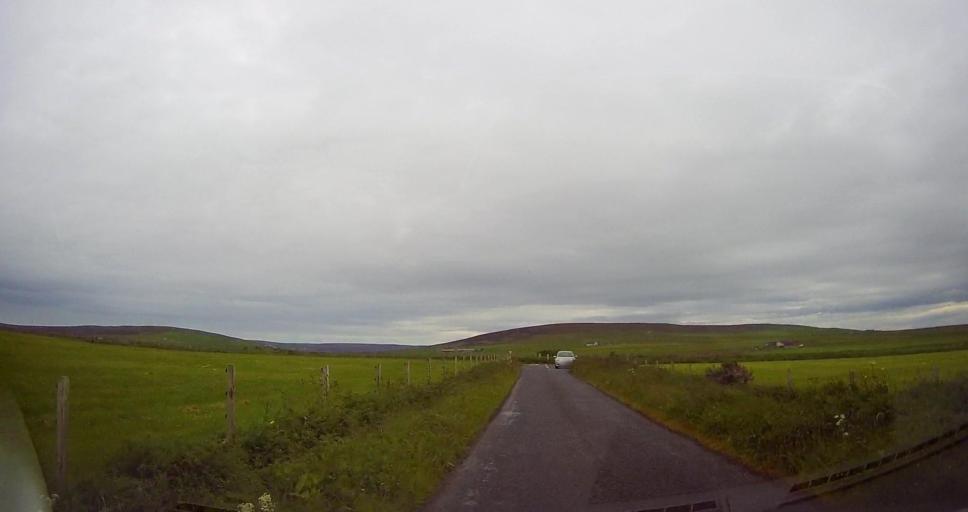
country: GB
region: Scotland
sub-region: Orkney Islands
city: Stromness
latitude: 59.1124
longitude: -3.2505
